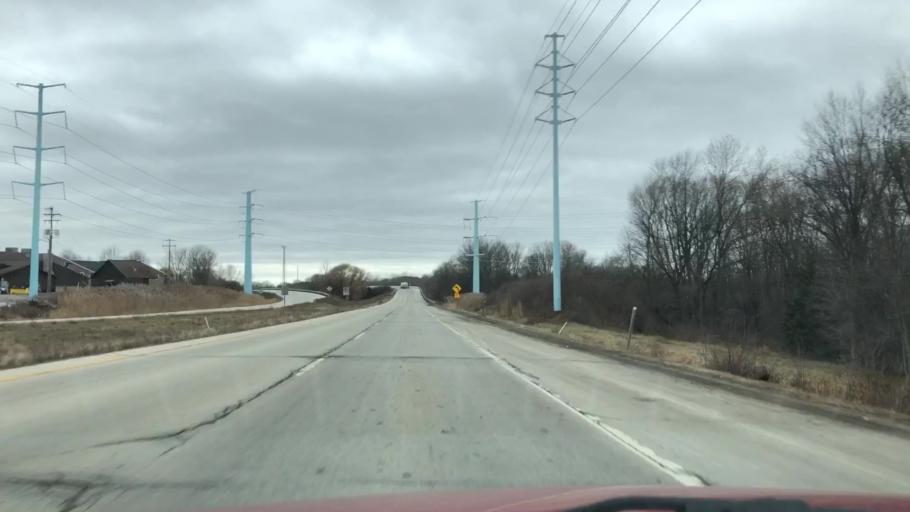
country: US
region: Wisconsin
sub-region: Brown County
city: De Pere
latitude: 44.4563
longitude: -88.0811
